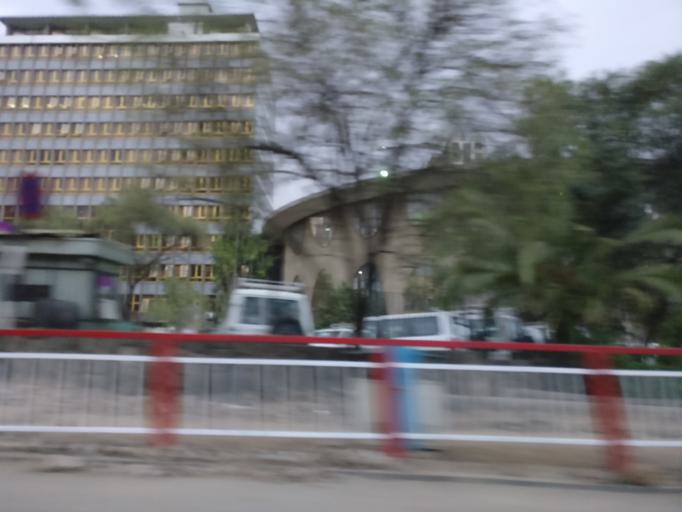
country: ET
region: Adis Abeba
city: Addis Ababa
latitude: 9.0171
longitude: 38.7516
